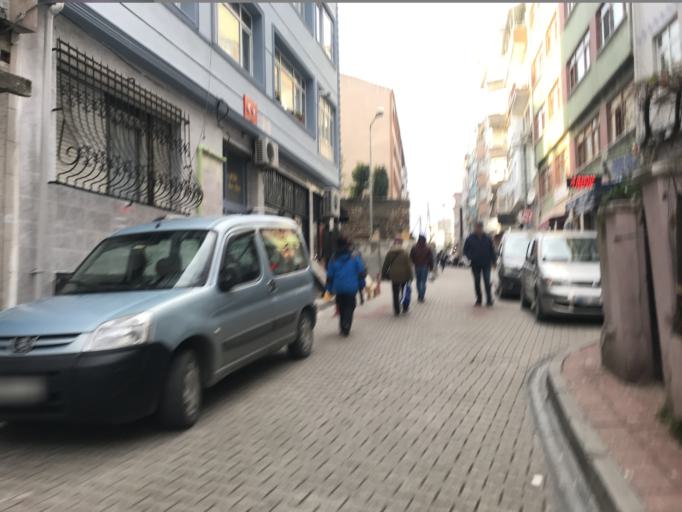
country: TR
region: Istanbul
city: Istanbul
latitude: 41.0238
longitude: 28.9412
